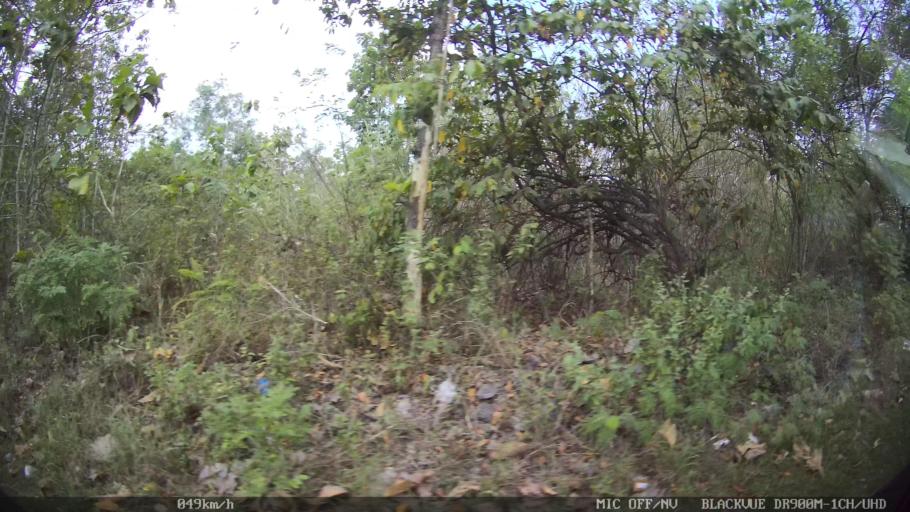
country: ID
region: Daerah Istimewa Yogyakarta
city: Bantul
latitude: -7.8579
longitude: 110.3095
